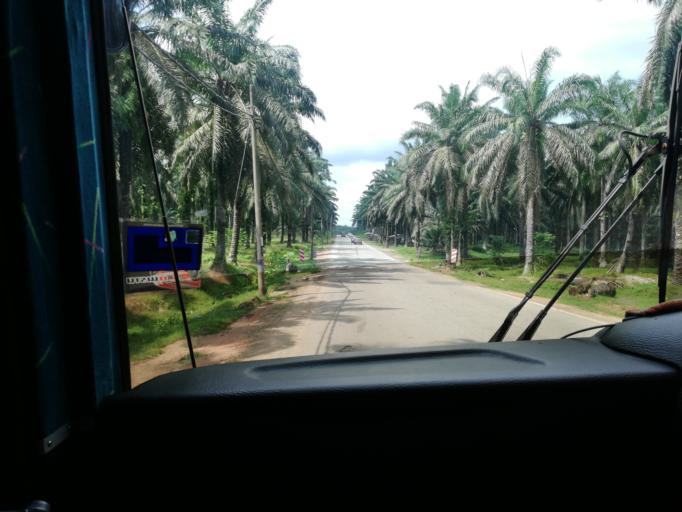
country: MY
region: Perak
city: Parit Buntar
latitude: 5.1554
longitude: 100.5930
